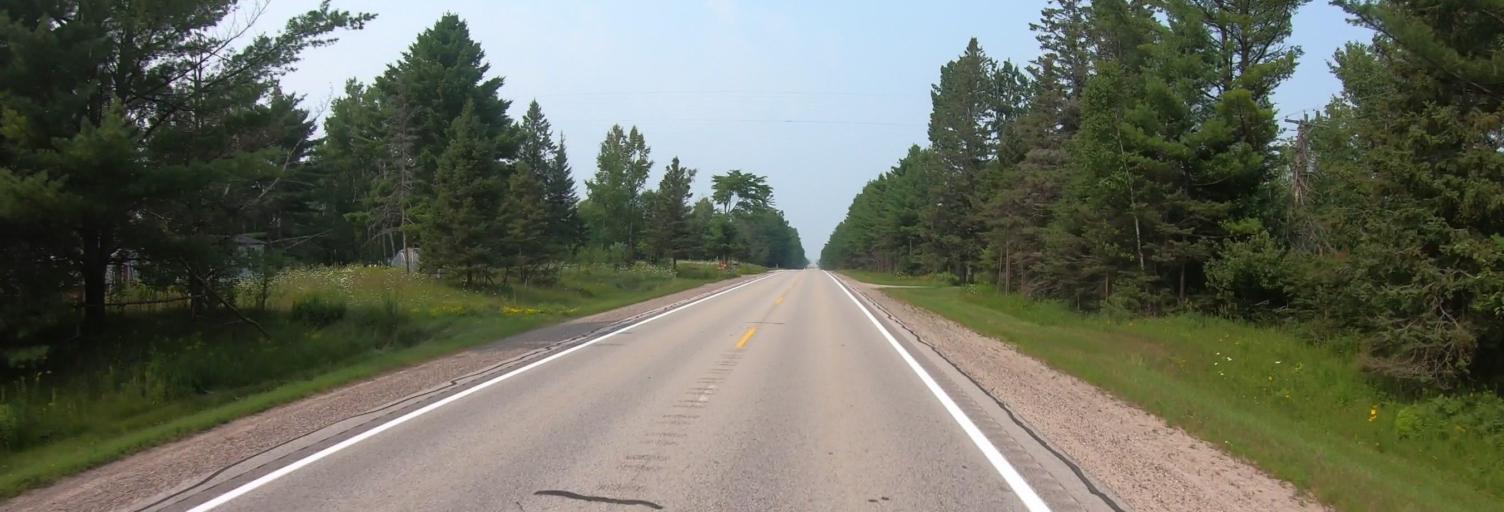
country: US
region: Michigan
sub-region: Chippewa County
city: Sault Ste. Marie
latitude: 46.2448
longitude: -84.3634
